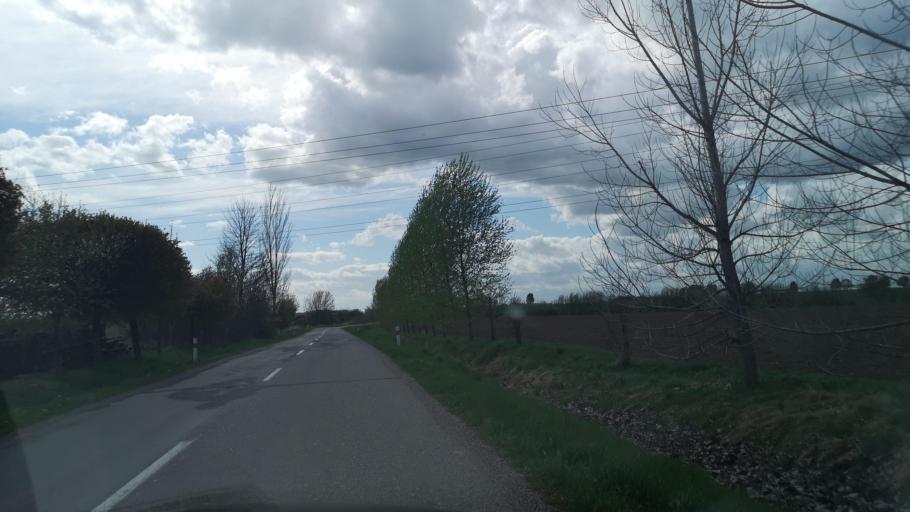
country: SK
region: Nitriansky
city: Zlate Moravce
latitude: 48.3170
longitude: 18.3539
